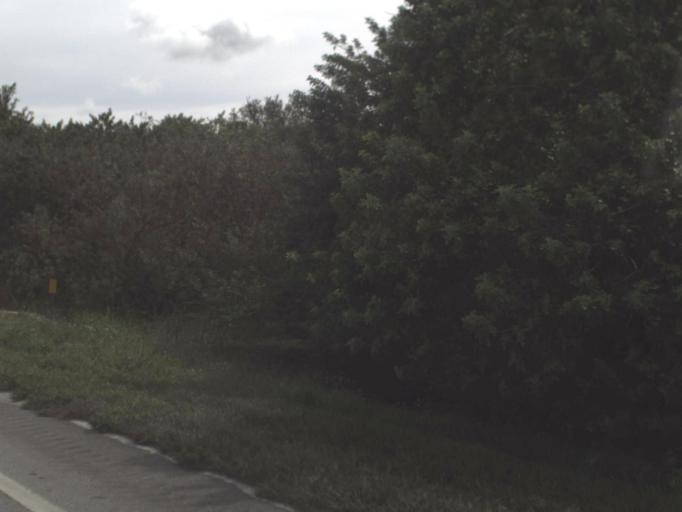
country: US
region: Florida
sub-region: Okeechobee County
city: Taylor Creek
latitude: 27.2568
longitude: -80.7609
